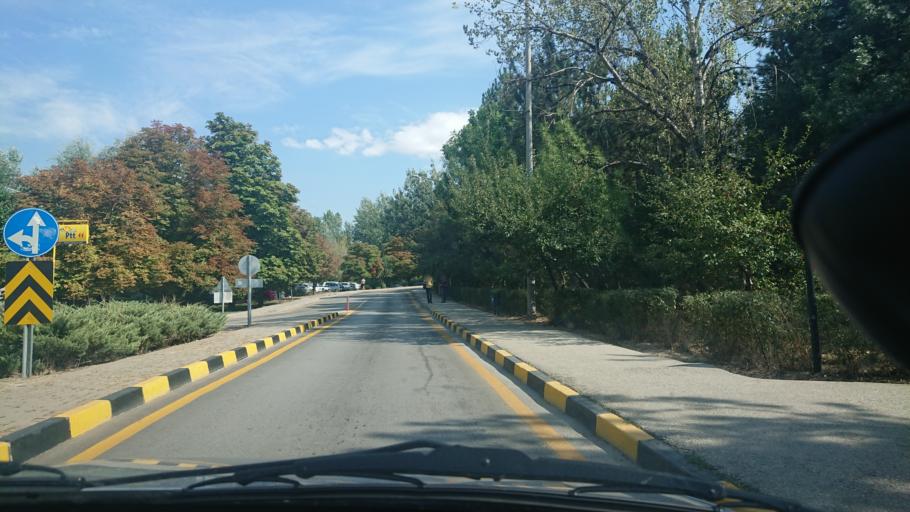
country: TR
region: Ankara
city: Ankara
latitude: 39.8914
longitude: 32.7890
